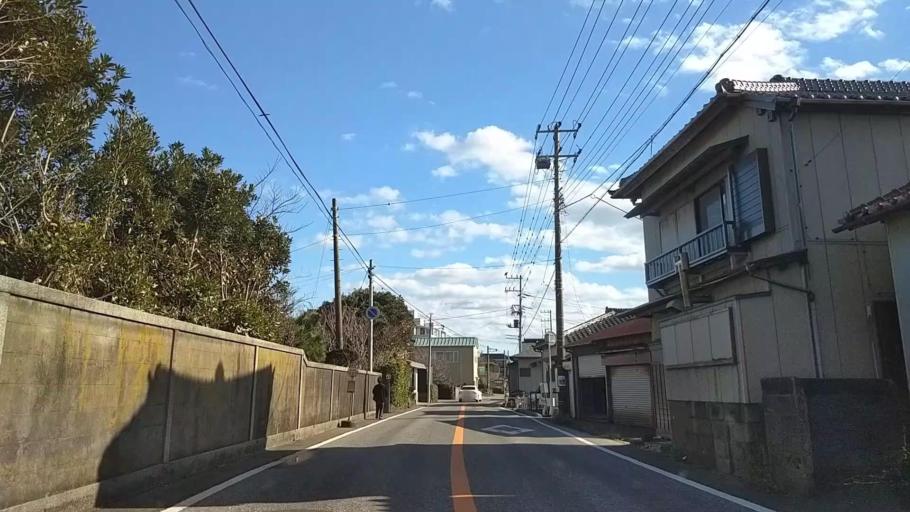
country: JP
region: Chiba
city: Tateyama
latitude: 35.0268
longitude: 139.8445
